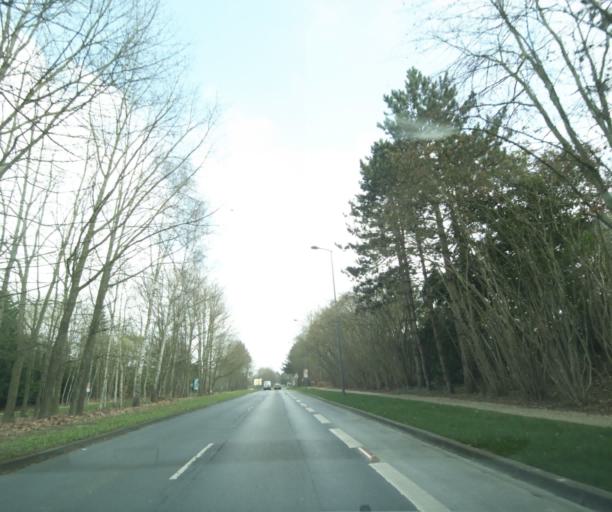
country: FR
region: Ile-de-France
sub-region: Departement du Val-d'Oise
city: Courdimanche
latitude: 49.0418
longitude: 2.0174
